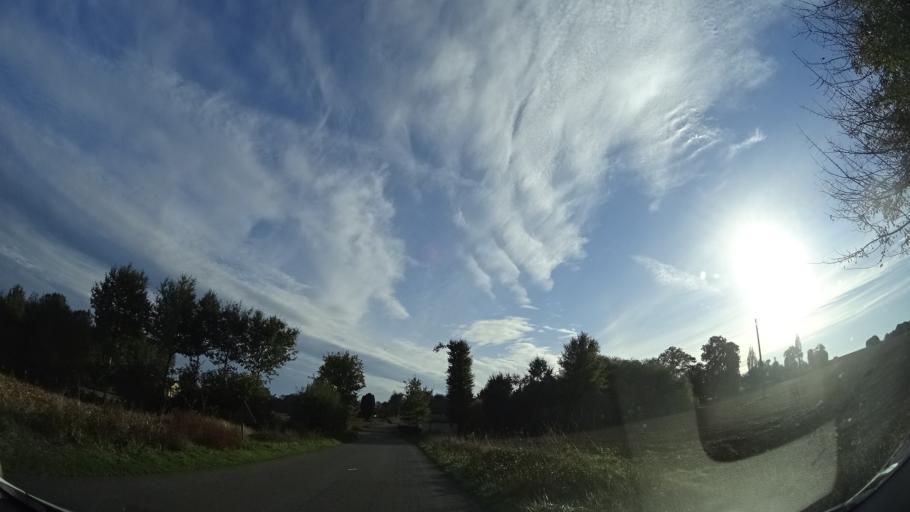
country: FR
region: Brittany
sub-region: Departement d'Ille-et-Vilaine
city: Geveze
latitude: 48.2073
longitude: -1.7910
